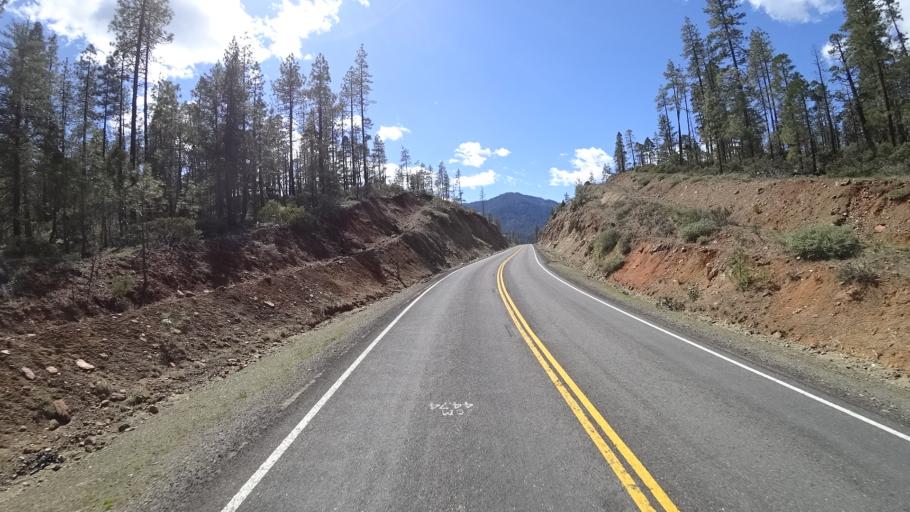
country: US
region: California
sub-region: Trinity County
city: Weaverville
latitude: 40.8498
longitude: -122.8532
